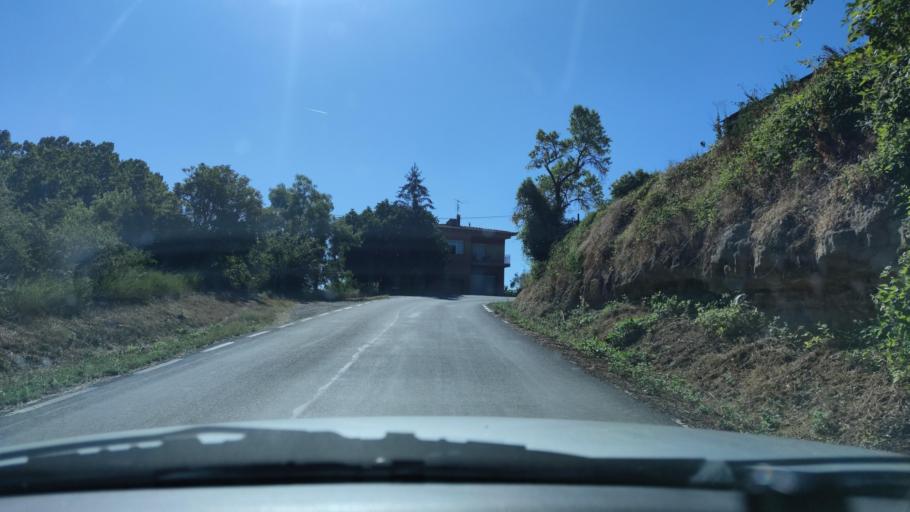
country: ES
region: Catalonia
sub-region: Provincia de Lleida
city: Solsona
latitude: 41.9852
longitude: 1.5052
